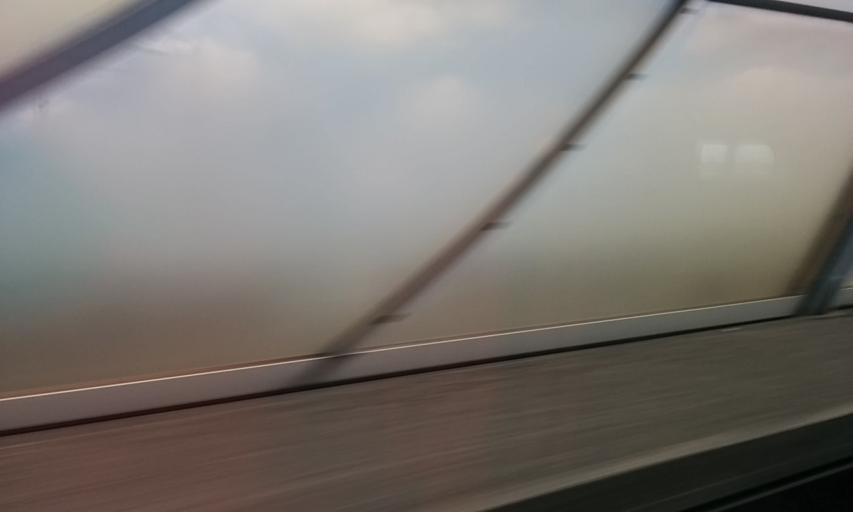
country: JP
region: Tochigi
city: Oyama
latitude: 36.2942
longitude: 139.7920
